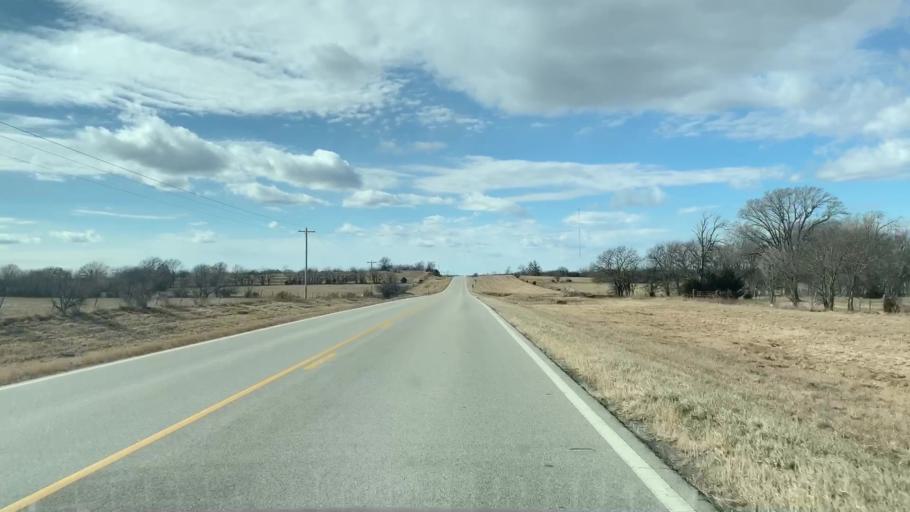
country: US
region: Kansas
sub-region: Neosho County
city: Erie
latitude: 37.5292
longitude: -95.3666
